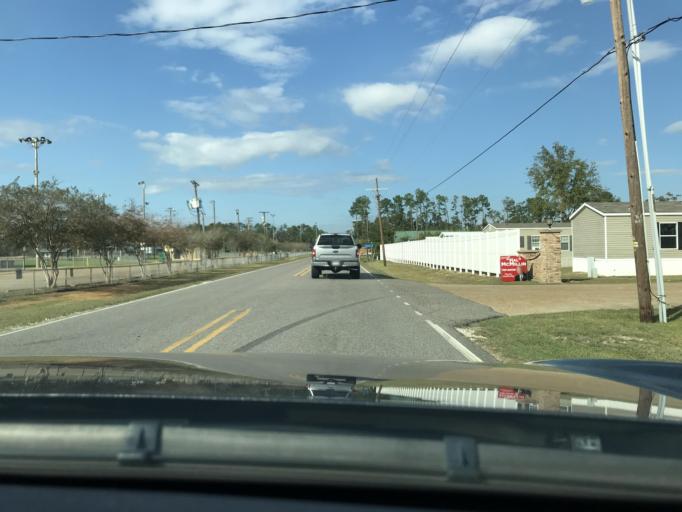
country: US
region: Louisiana
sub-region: Calcasieu Parish
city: Westlake
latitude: 30.2796
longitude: -93.2582
